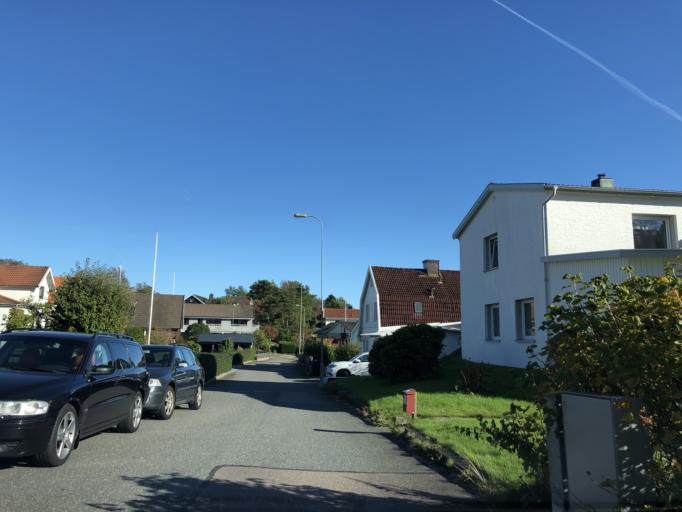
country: SE
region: Vaestra Goetaland
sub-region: Goteborg
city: Majorna
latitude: 57.6540
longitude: 11.8595
